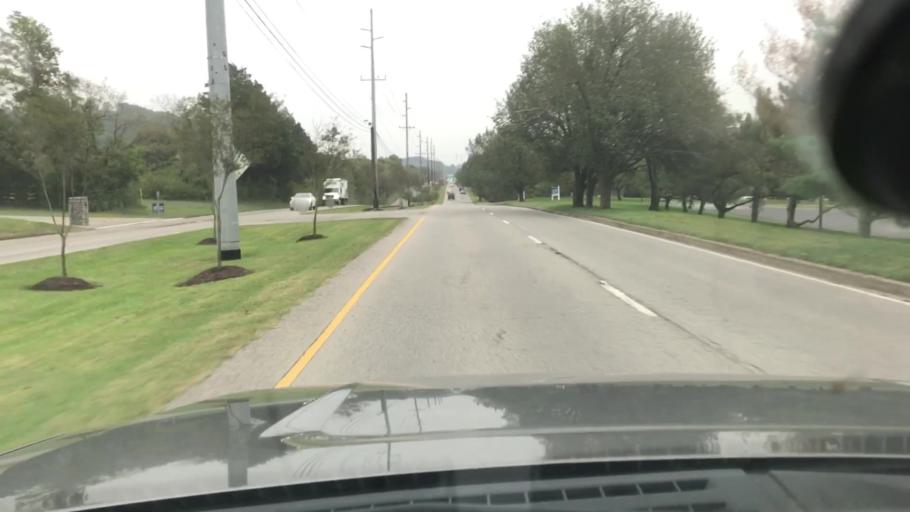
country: US
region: Tennessee
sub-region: Williamson County
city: Brentwood
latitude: 36.0387
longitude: -86.8078
